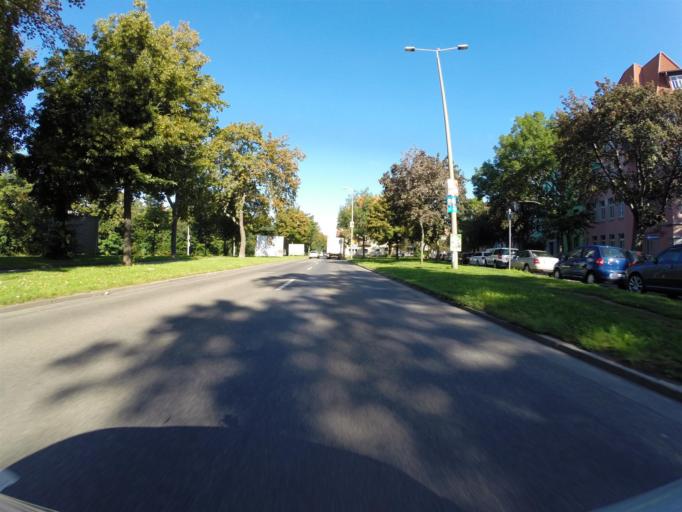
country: DE
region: Thuringia
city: Erfurt
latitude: 50.9815
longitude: 11.0393
